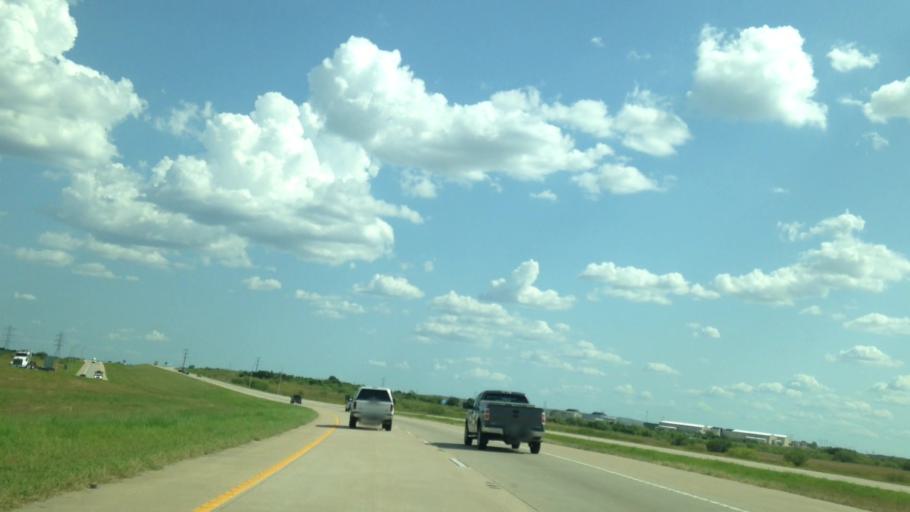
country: US
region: Texas
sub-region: Travis County
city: Onion Creek
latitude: 30.1327
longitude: -97.6662
